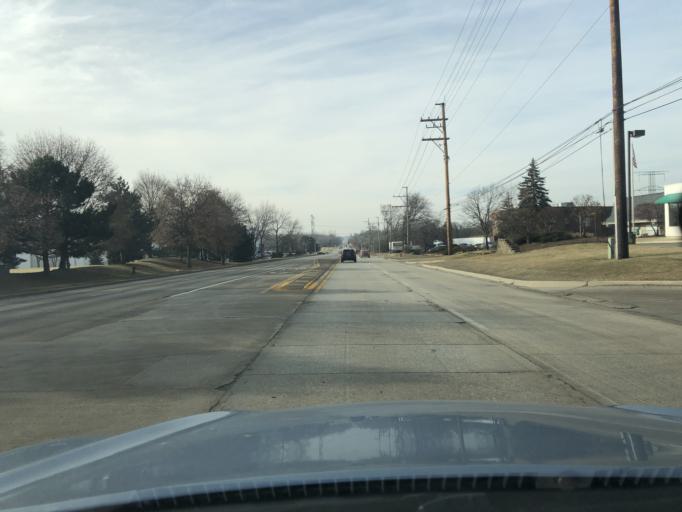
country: US
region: Illinois
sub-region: Cook County
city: Elk Grove Village
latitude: 41.9929
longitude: -87.9852
